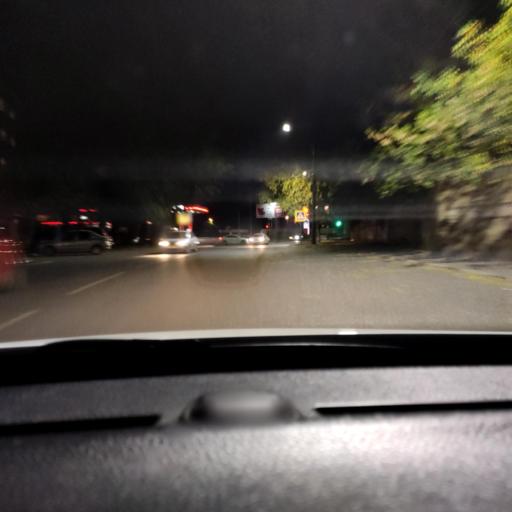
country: RU
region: Voronezj
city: Voronezh
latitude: 51.6828
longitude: 39.2028
